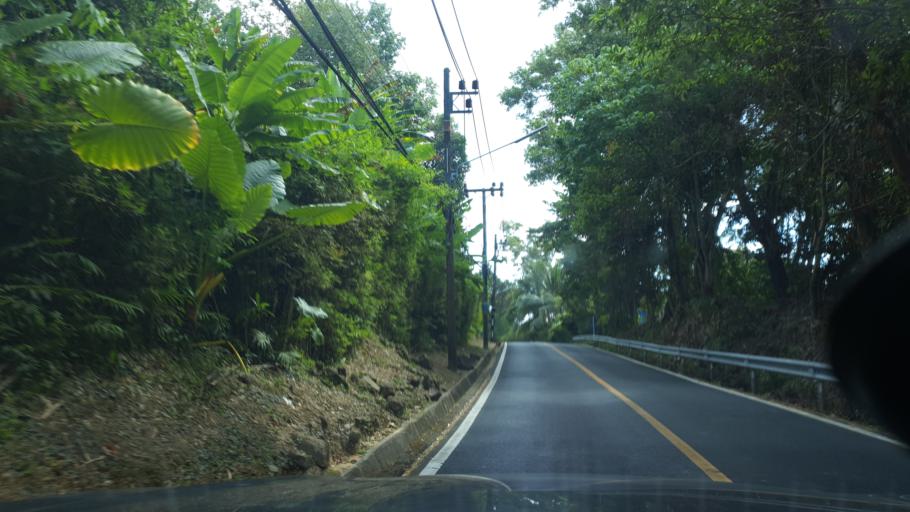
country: TH
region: Phuket
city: Thalang
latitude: 8.0520
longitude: 98.2775
